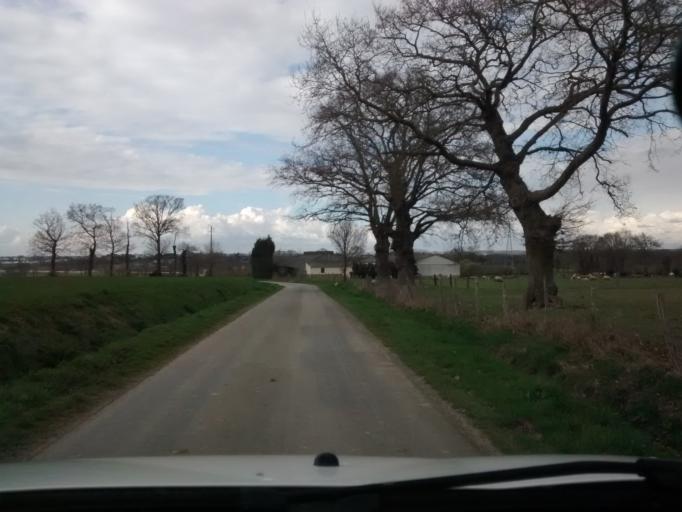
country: FR
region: Brittany
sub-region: Departement d'Ille-et-Vilaine
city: Cesson-Sevigne
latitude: 48.0987
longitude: -1.5774
